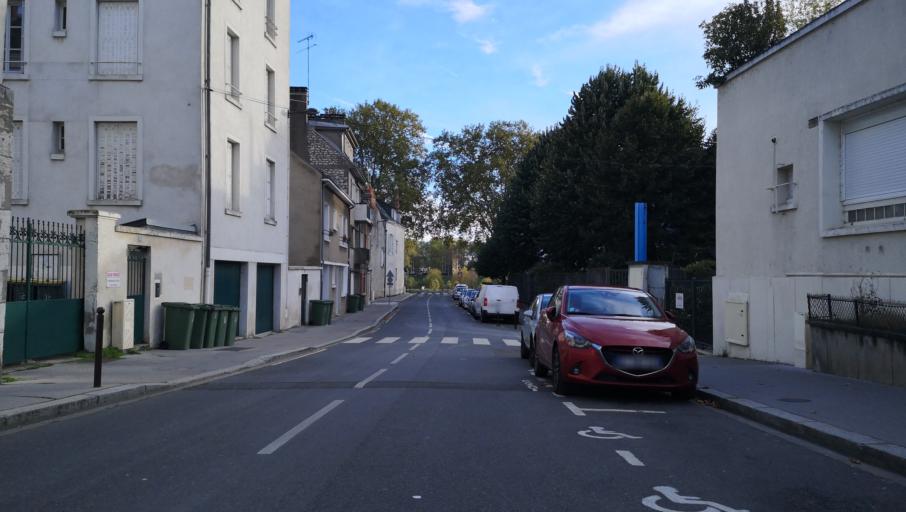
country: FR
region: Centre
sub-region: Departement du Loiret
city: Orleans
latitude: 47.8990
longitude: 1.8994
